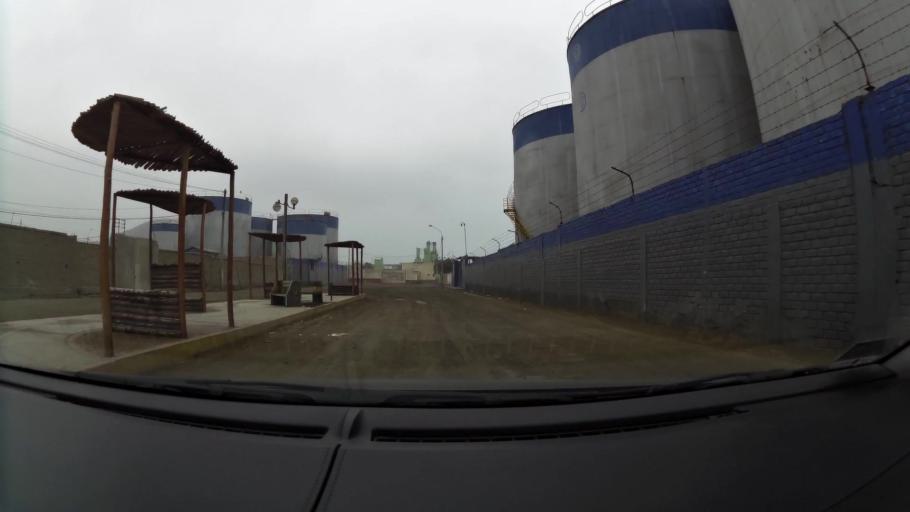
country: PE
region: Lima
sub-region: Provincia de Huaral
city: Chancay
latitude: -11.5751
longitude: -77.2701
